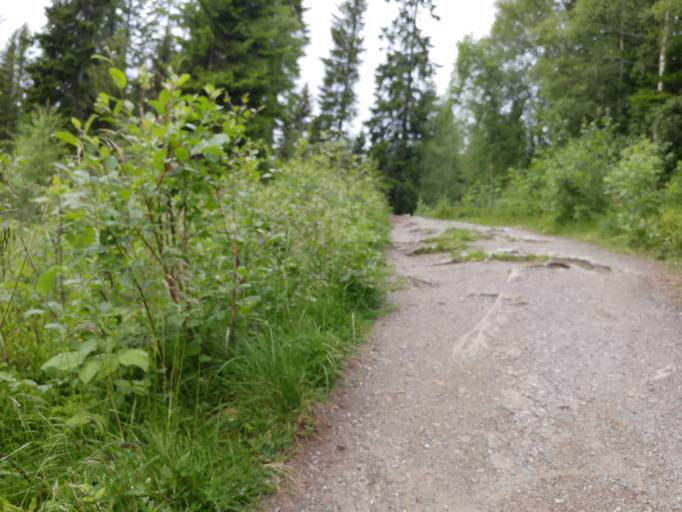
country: NO
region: Sor-Trondelag
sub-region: Melhus
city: Melhus
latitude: 63.4008
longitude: 10.2620
